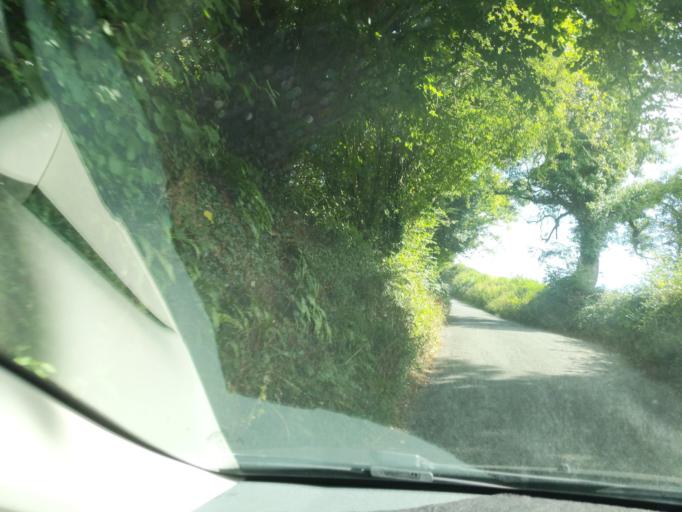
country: GB
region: England
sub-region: Cornwall
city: Torpoint
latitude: 50.3563
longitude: -4.2238
